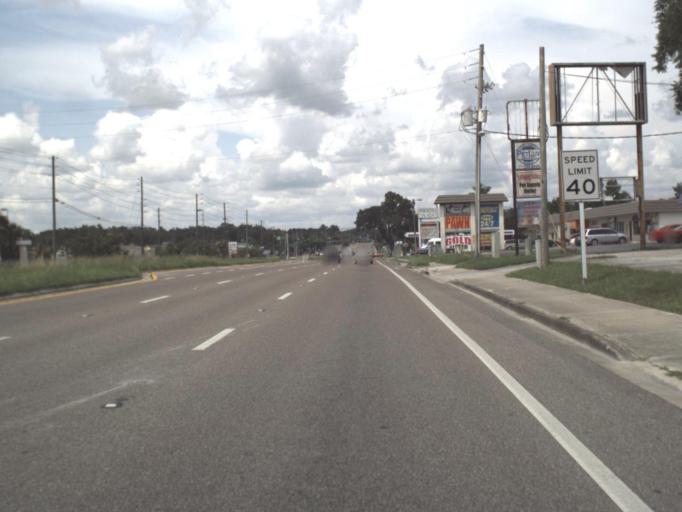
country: US
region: Florida
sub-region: Hernando County
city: South Brooksville
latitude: 28.5365
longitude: -82.4057
